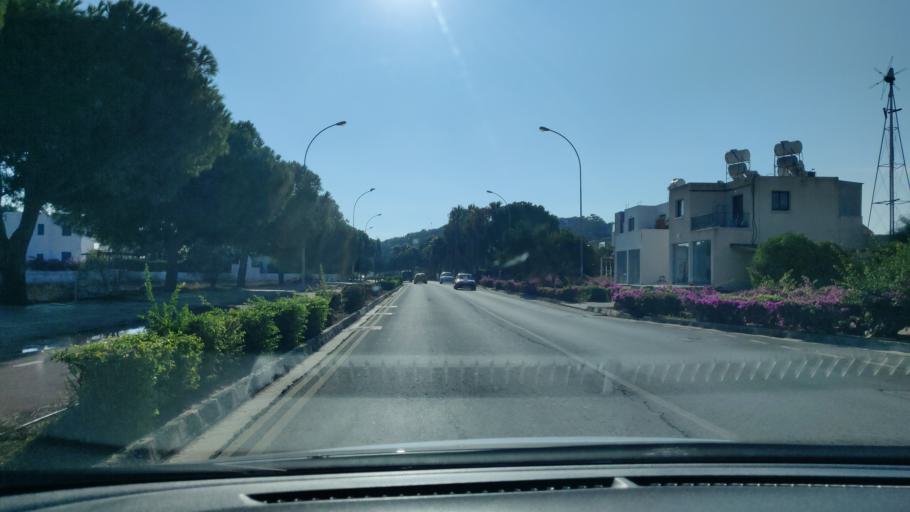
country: CY
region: Ammochostos
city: Protaras
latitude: 35.0127
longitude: 34.0512
